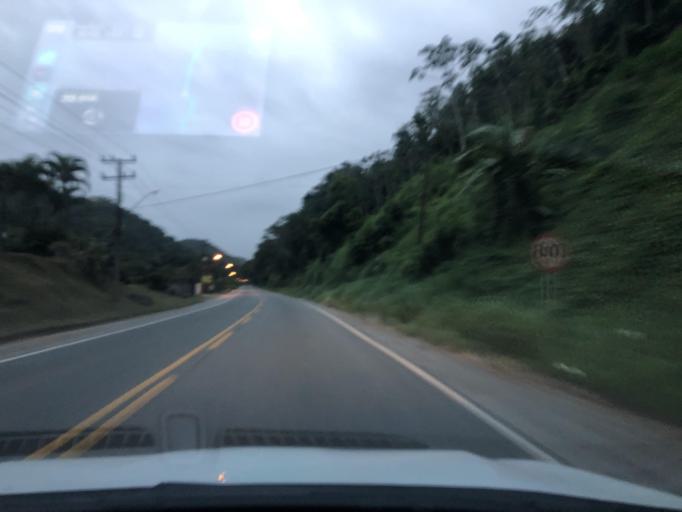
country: BR
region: Santa Catarina
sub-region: Pomerode
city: Pomerode
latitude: -26.7132
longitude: -49.0566
